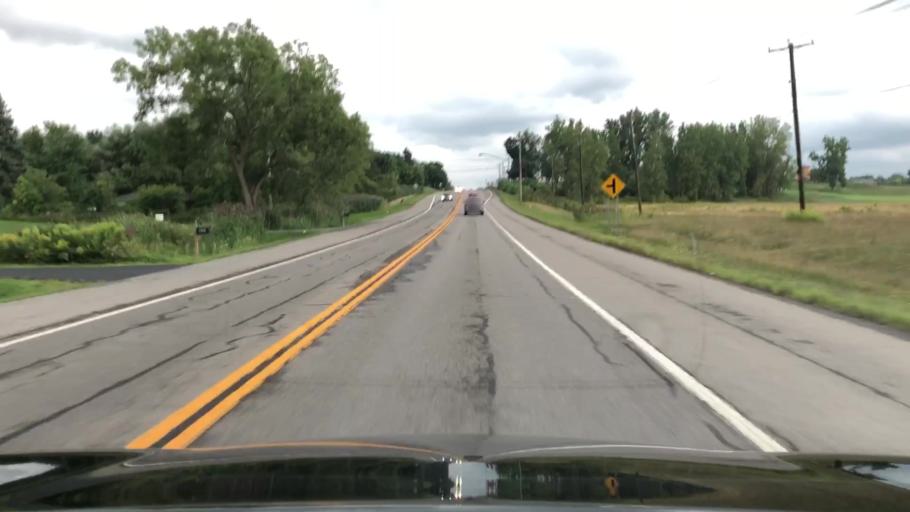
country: US
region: New York
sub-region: Erie County
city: Orchard Park
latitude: 42.8080
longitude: -78.6970
